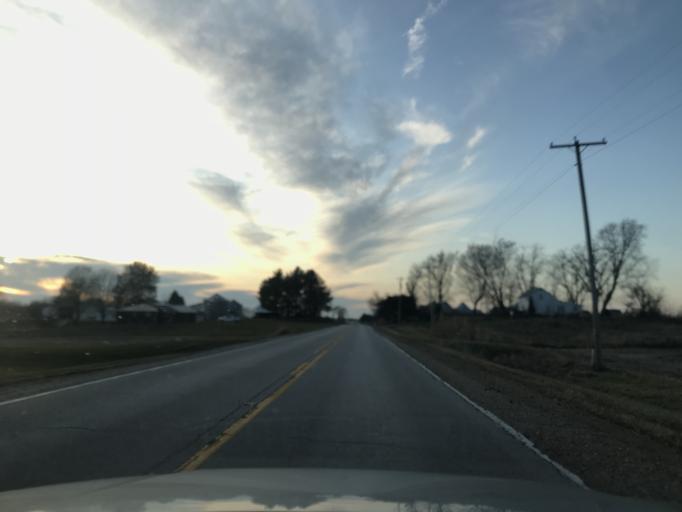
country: US
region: Illinois
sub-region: Warren County
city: Monmouth
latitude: 41.0250
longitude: -90.7690
